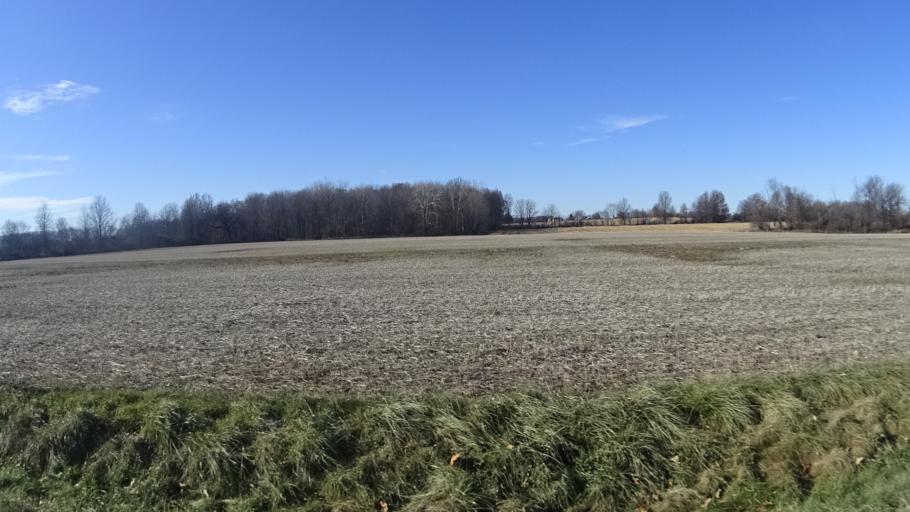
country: US
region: Ohio
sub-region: Lorain County
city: South Amherst
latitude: 41.3316
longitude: -82.2881
